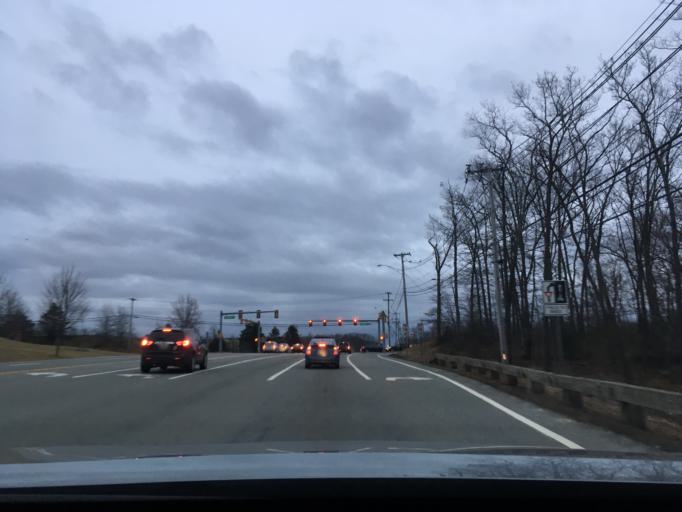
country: US
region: Rhode Island
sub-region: Providence County
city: Smithfield
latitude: 41.9184
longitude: -71.5215
